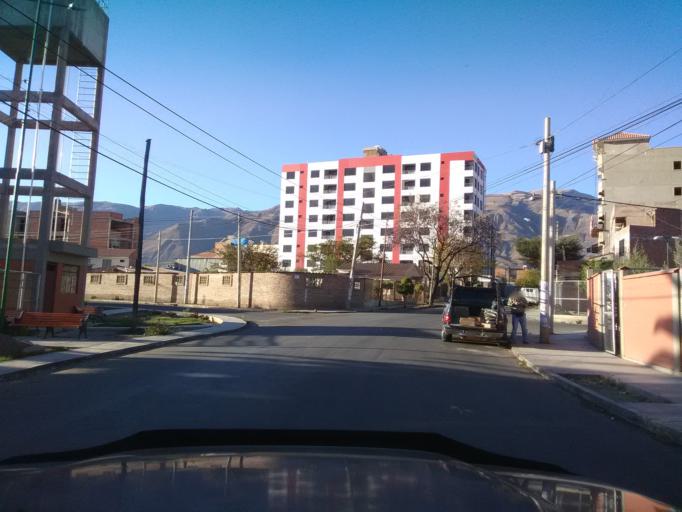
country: BO
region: Cochabamba
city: Cochabamba
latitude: -17.3668
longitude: -66.1881
